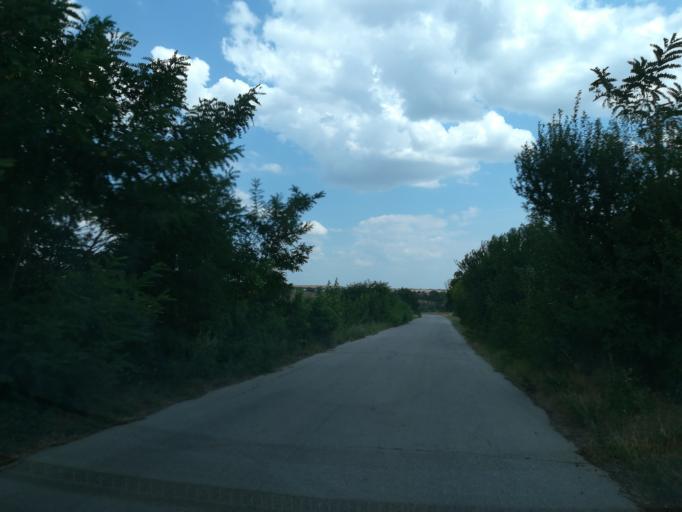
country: BG
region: Khaskovo
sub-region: Obshtina Mineralni Bani
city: Mineralni Bani
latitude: 41.9810
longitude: 25.1625
